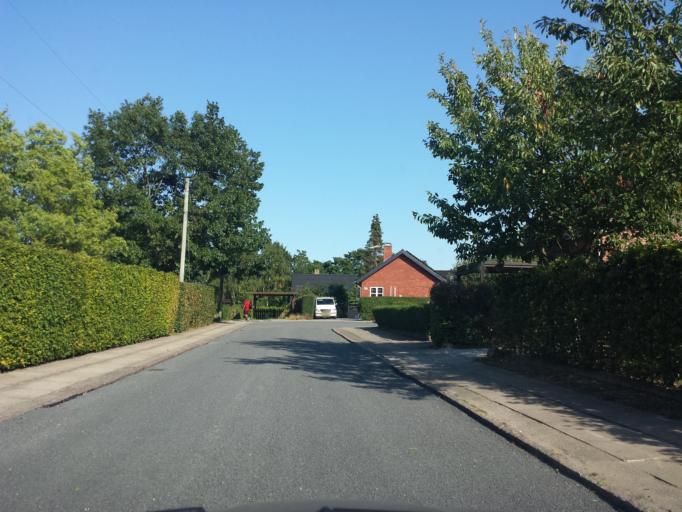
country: DK
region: Capital Region
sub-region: Herlev Kommune
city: Herlev
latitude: 55.7255
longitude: 12.4129
